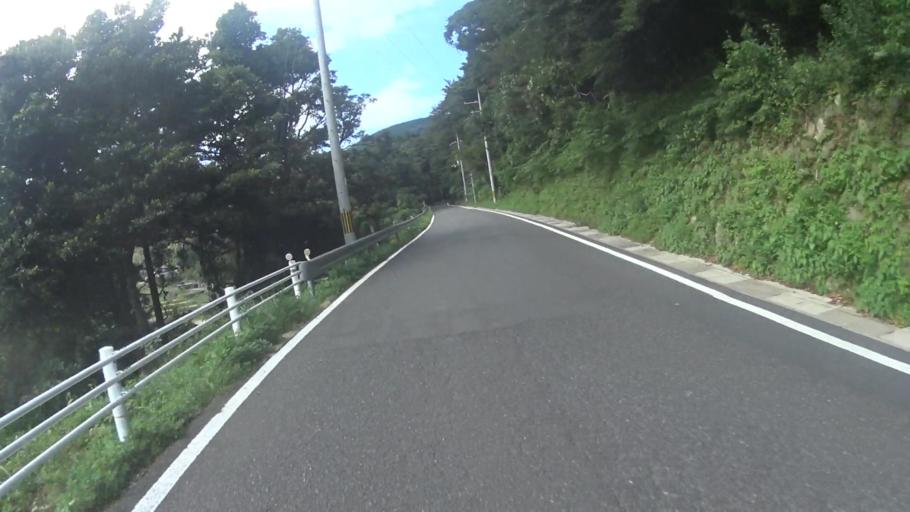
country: JP
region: Kyoto
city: Miyazu
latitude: 35.7422
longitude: 135.2450
